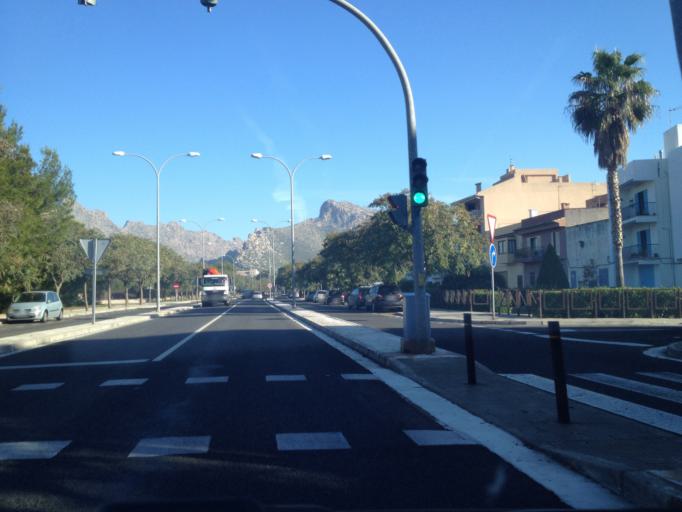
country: ES
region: Balearic Islands
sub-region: Illes Balears
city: Pollenca
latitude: 39.9057
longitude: 3.0760
